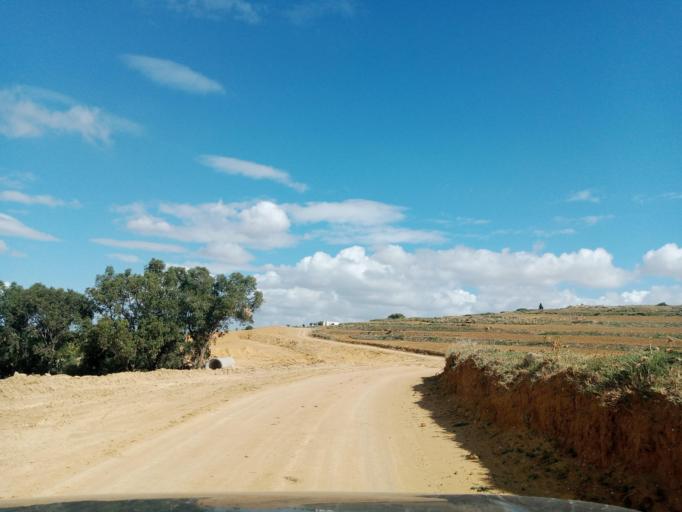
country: TN
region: Tunis
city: Oued Lill
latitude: 36.8144
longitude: 9.9984
